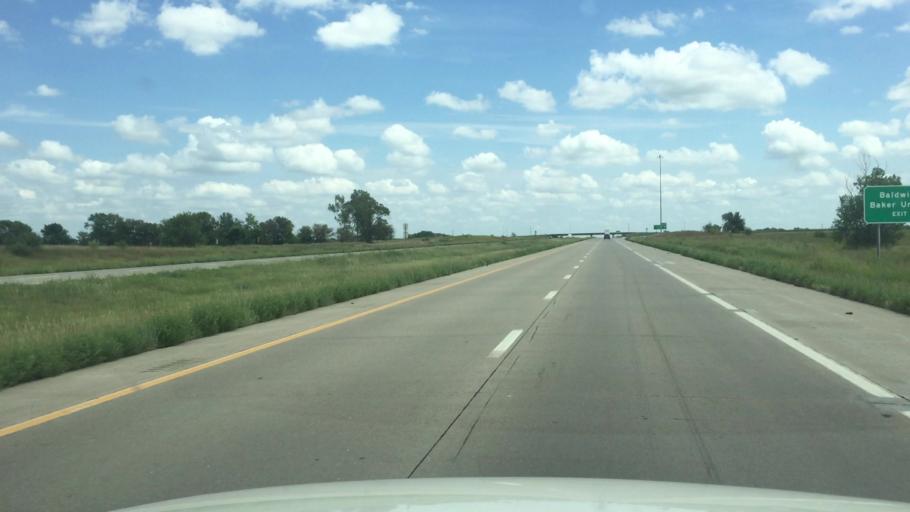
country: US
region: Kansas
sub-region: Franklin County
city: Wellsville
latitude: 38.6666
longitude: -95.1652
